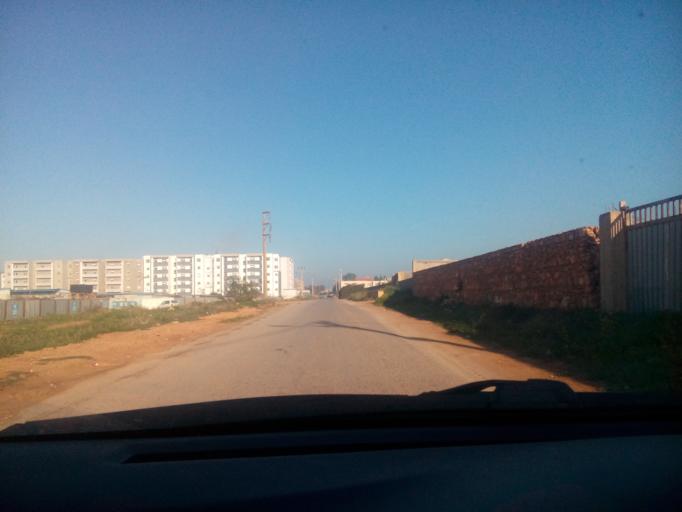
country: DZ
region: Oran
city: Bir el Djir
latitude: 35.7524
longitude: -0.5290
